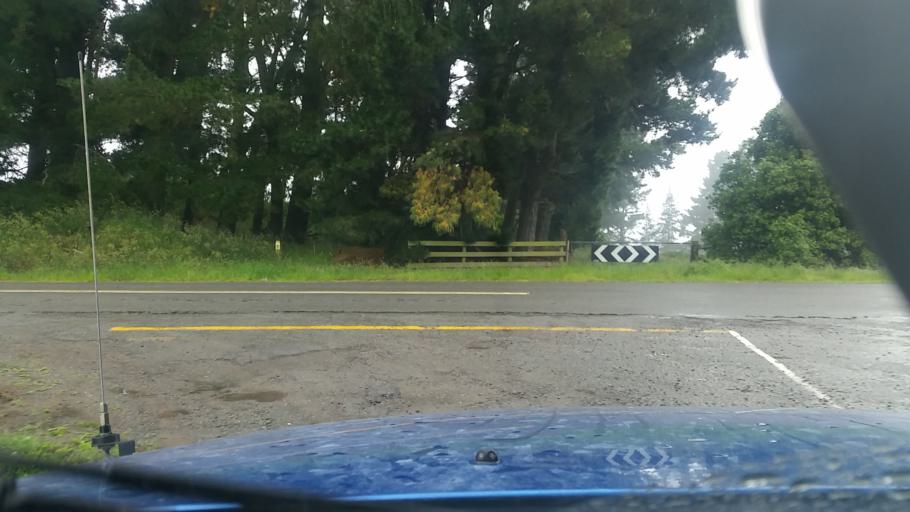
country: NZ
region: Canterbury
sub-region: Ashburton District
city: Rakaia
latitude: -43.7114
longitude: 171.9349
